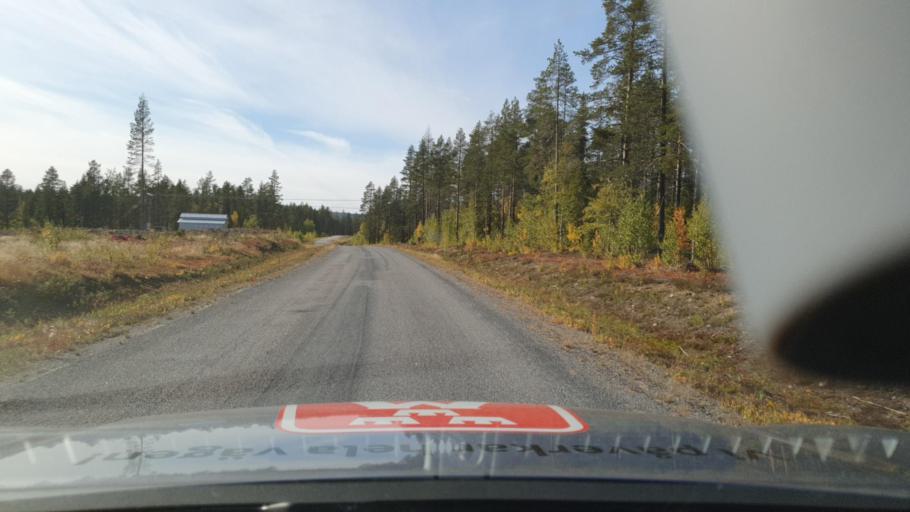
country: SE
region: Norrbotten
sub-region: Jokkmokks Kommun
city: Jokkmokk
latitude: 66.1876
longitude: 19.9663
